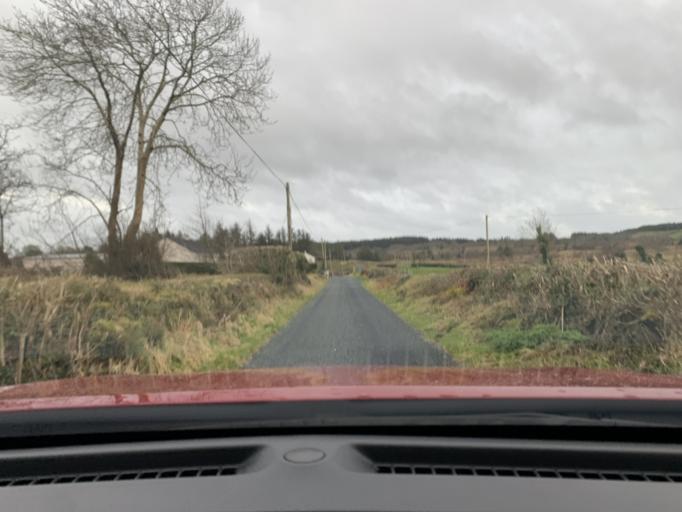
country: IE
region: Connaught
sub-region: Roscommon
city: Ballaghaderreen
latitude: 53.9680
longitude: -8.5177
